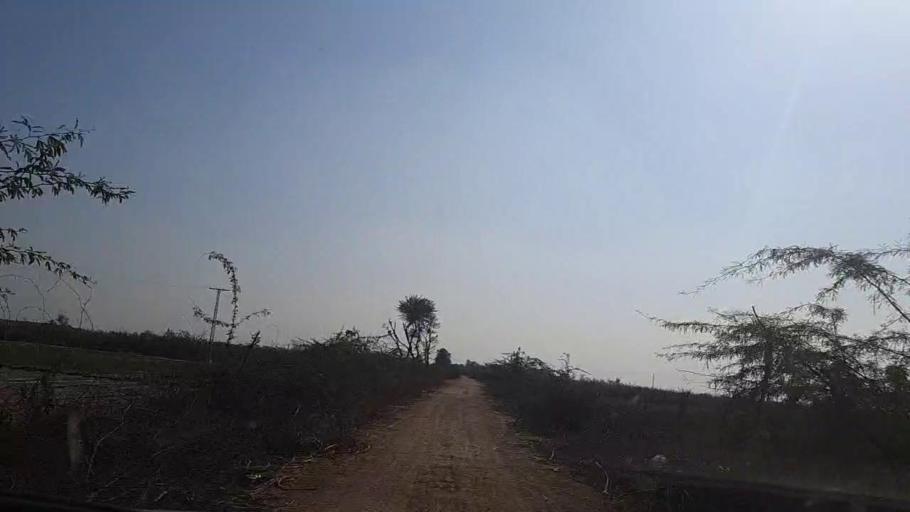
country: PK
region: Sindh
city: Sakrand
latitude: 26.0799
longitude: 68.3694
